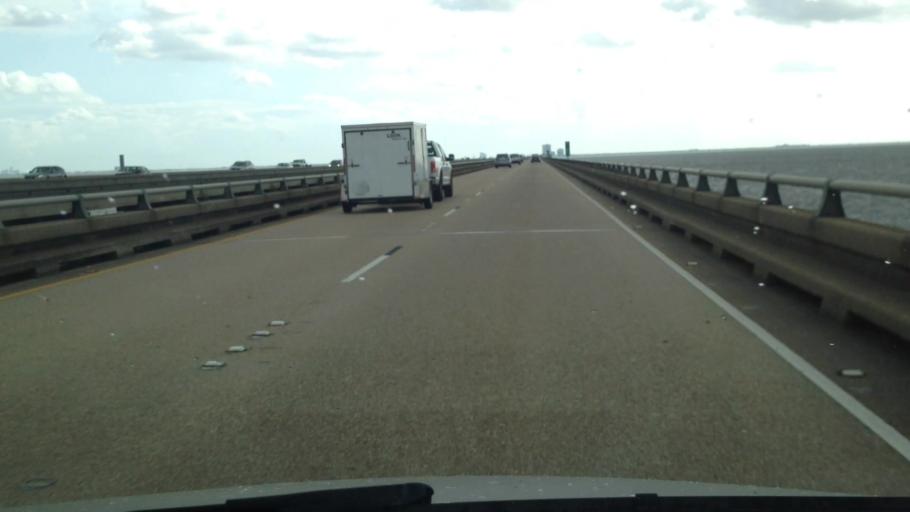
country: US
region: Louisiana
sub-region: Jefferson Parish
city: Metairie
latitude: 30.1002
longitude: -90.1404
